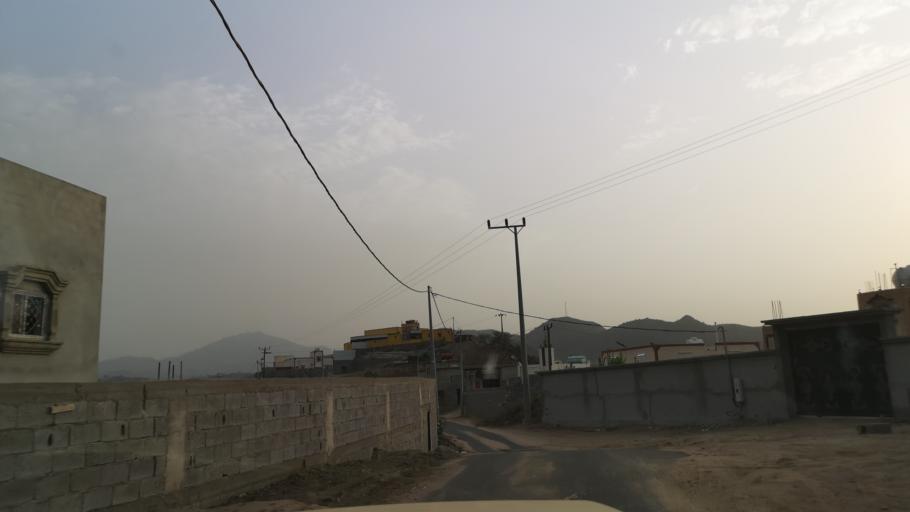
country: YE
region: Sa'dah
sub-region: Monabbih
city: Suq al Khamis
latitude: 17.3757
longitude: 43.1272
